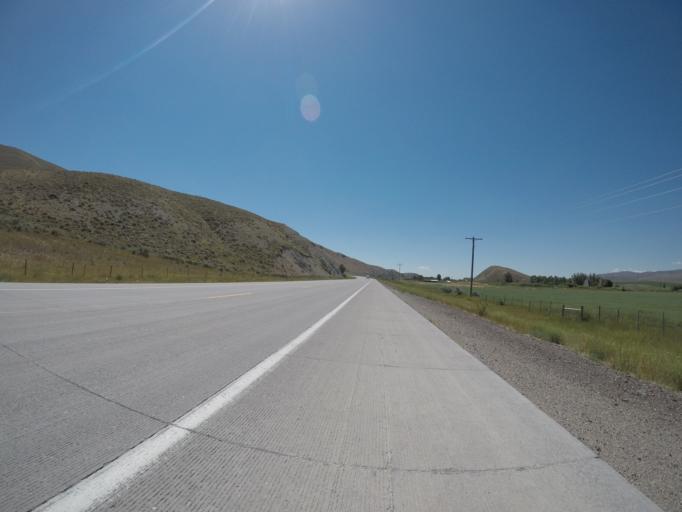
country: US
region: Idaho
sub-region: Bear Lake County
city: Montpelier
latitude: 42.1451
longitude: -110.9759
